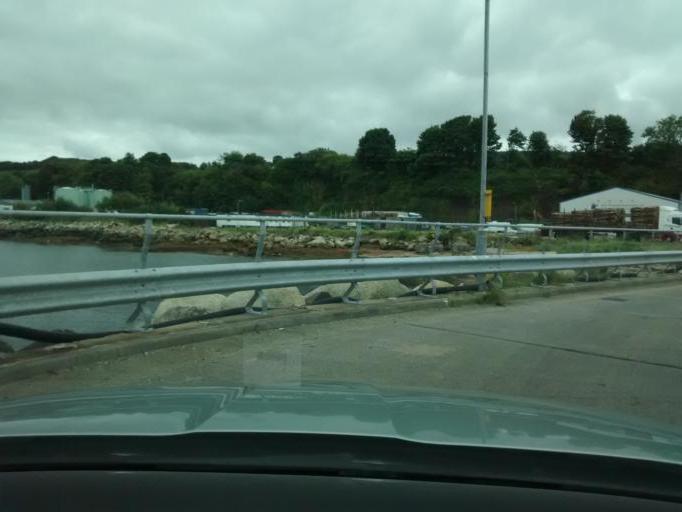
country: GB
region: Scotland
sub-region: North Ayrshire
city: Lamlash
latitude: 55.5772
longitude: -5.1374
